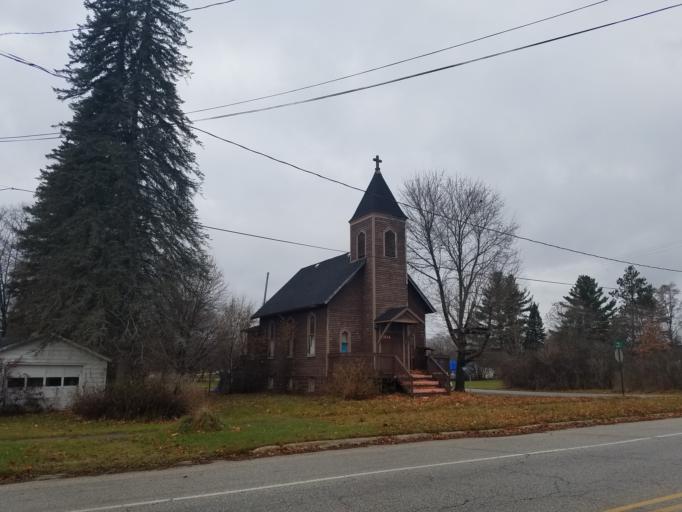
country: US
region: Michigan
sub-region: Osceola County
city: Evart
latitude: 43.8975
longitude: -85.2596
